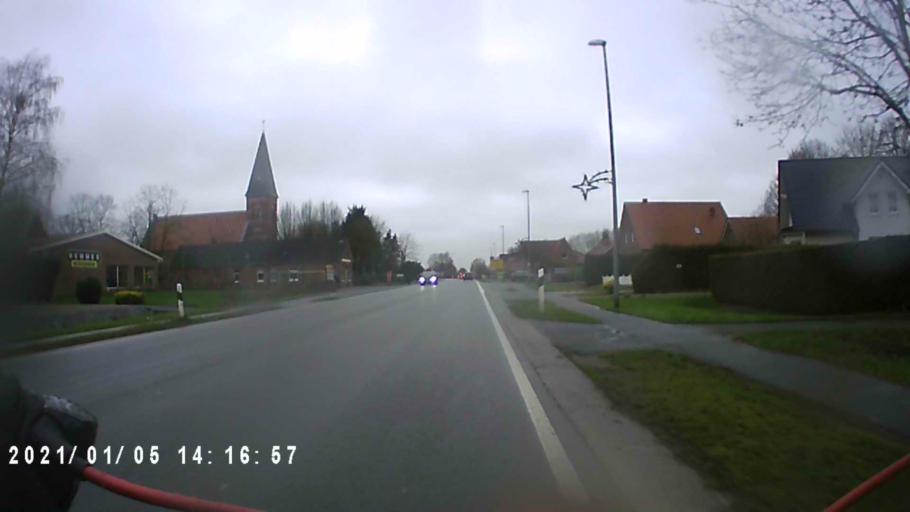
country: DE
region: Lower Saxony
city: Bunde
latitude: 53.1760
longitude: 7.3054
